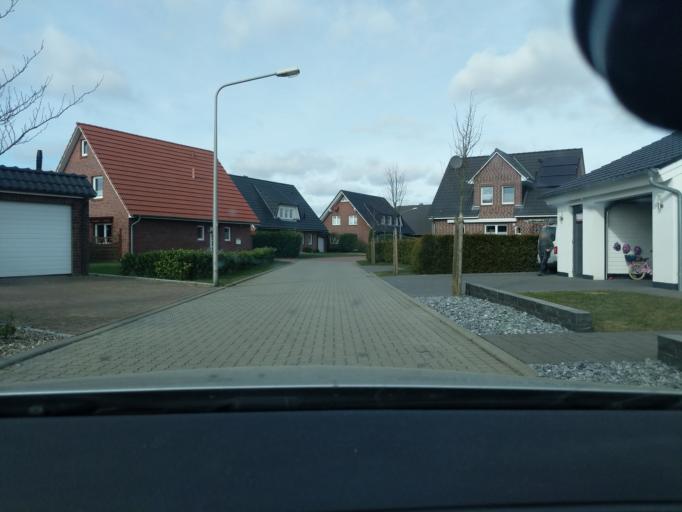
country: DE
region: Lower Saxony
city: Drochtersen
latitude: 53.6832
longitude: 9.4283
